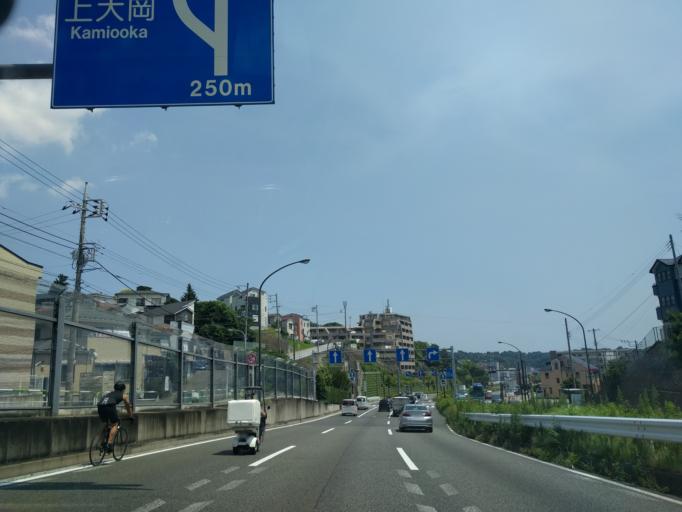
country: JP
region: Kanagawa
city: Yokohama
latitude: 35.3997
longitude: 139.5797
